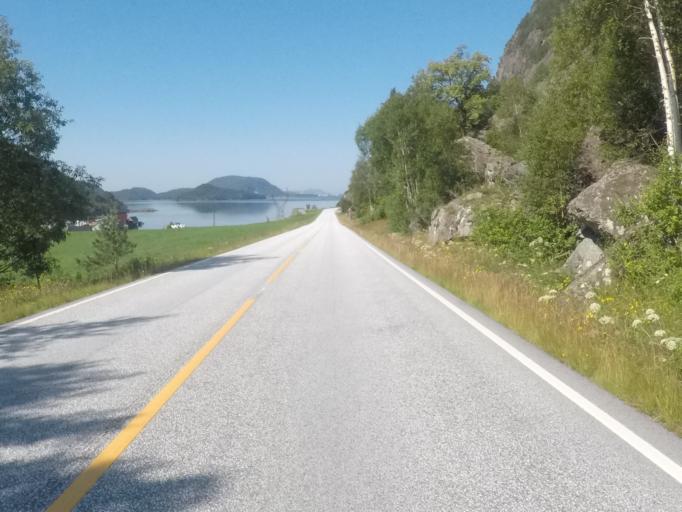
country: NO
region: Sogn og Fjordane
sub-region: Bremanger
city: Svelgen
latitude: 61.6368
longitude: 5.2446
